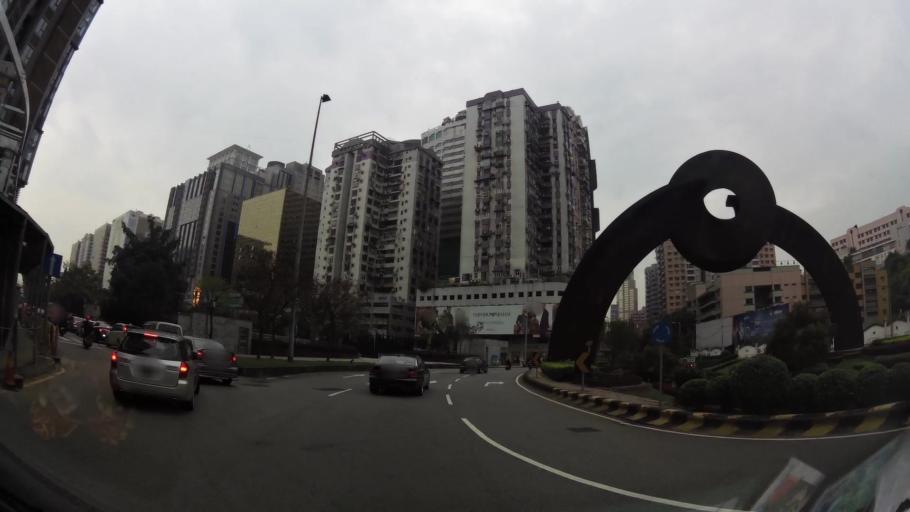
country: MO
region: Macau
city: Macau
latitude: 22.1935
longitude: 113.5492
